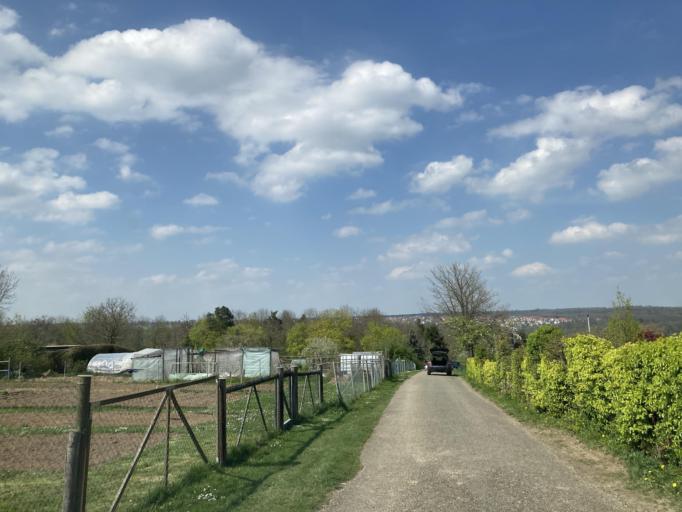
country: DE
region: Baden-Wuerttemberg
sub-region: Tuebingen Region
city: Kusterdingen
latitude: 48.5269
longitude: 9.1147
